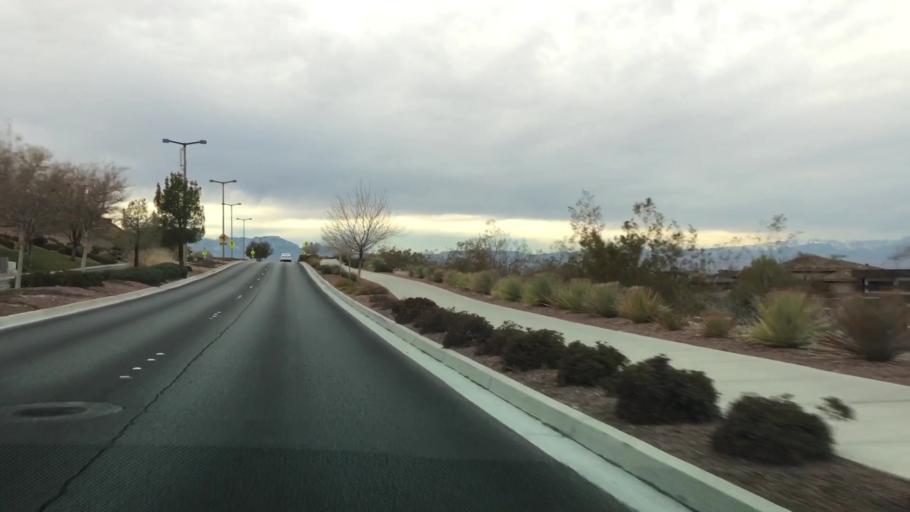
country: US
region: Nevada
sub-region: Clark County
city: Whitney
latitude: 35.9695
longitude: -115.1063
